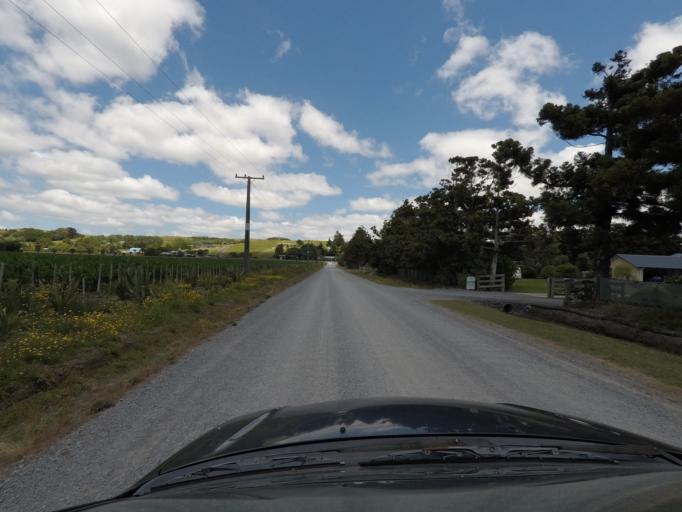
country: NZ
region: Northland
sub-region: Whangarei
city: Ruakaka
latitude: -35.9988
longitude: 174.4775
